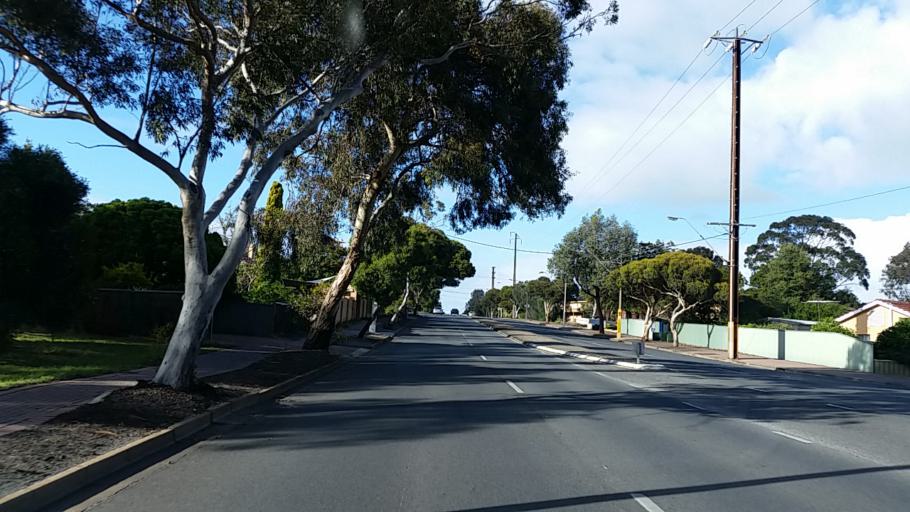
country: AU
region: South Australia
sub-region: Mitcham
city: Clapham
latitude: -35.0033
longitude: 138.5896
